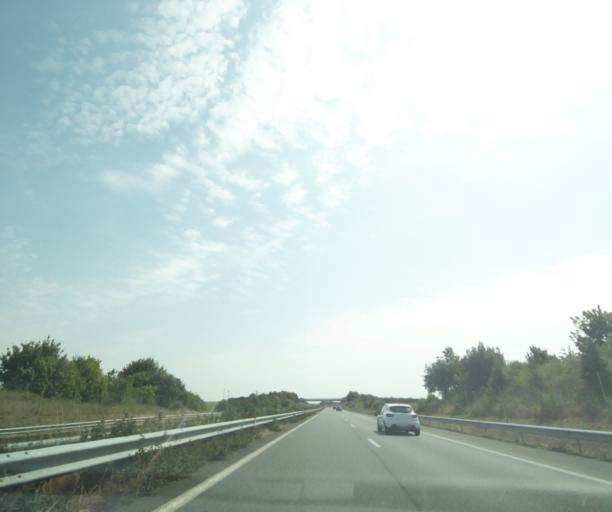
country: FR
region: Pays de la Loire
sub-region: Departement de la Vendee
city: Le Langon
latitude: 46.4787
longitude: -0.9430
